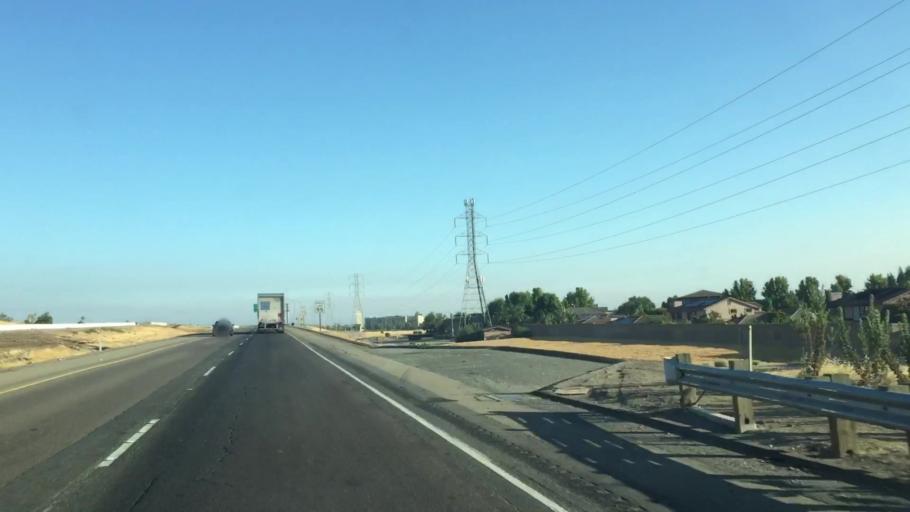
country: US
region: California
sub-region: Contra Costa County
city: Brentwood
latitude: 37.9373
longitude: -121.7384
